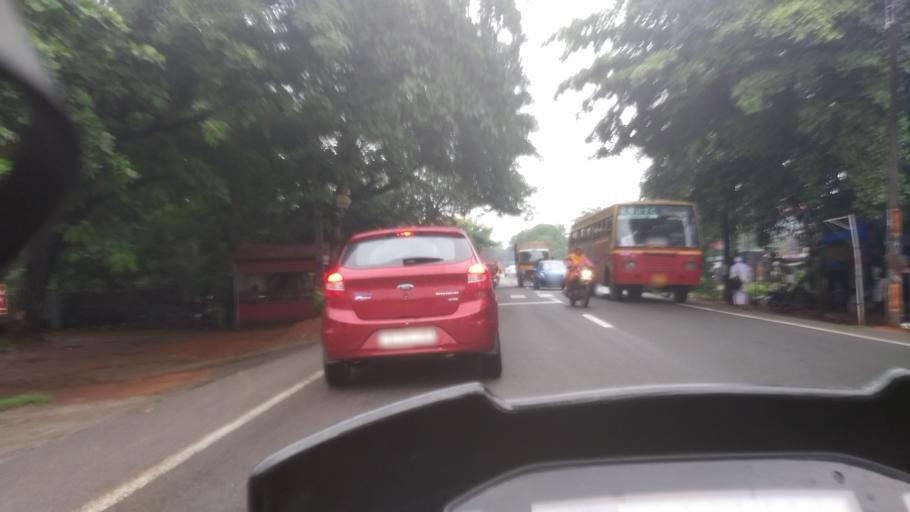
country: IN
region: Kerala
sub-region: Alappuzha
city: Kayankulam
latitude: 9.1871
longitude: 76.4887
